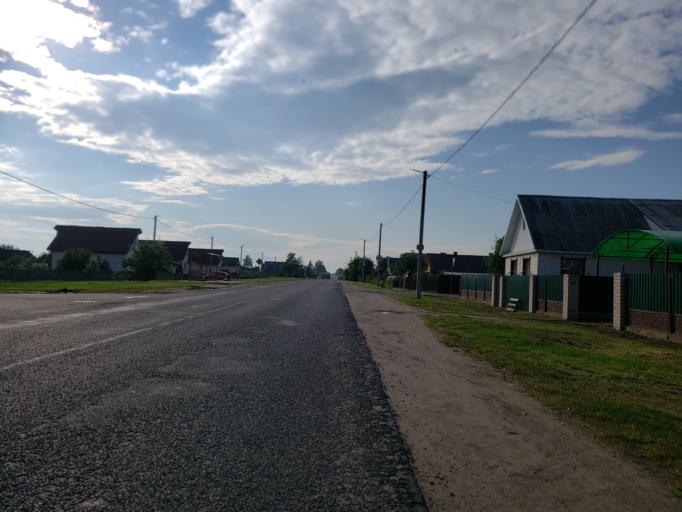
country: BY
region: Minsk
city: Chervyen'
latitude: 53.7002
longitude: 28.4463
